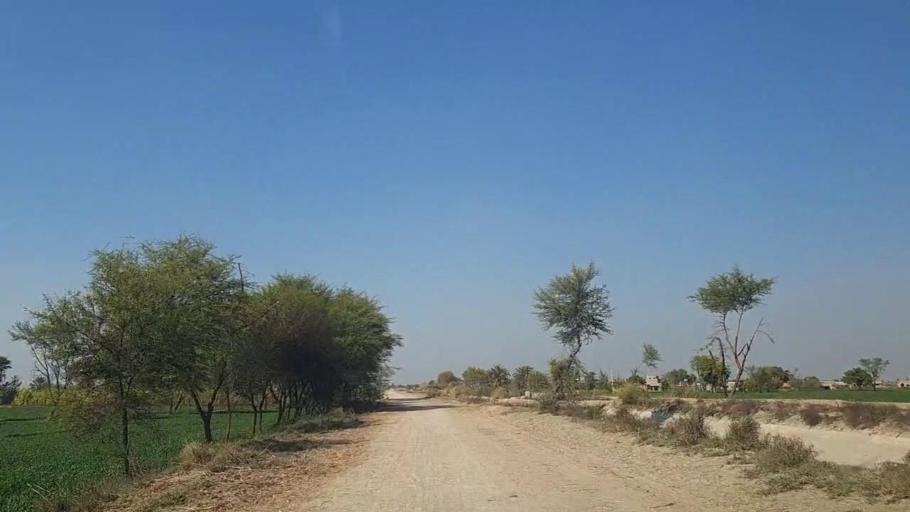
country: PK
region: Sindh
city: Sakrand
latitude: 26.2726
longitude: 68.2203
